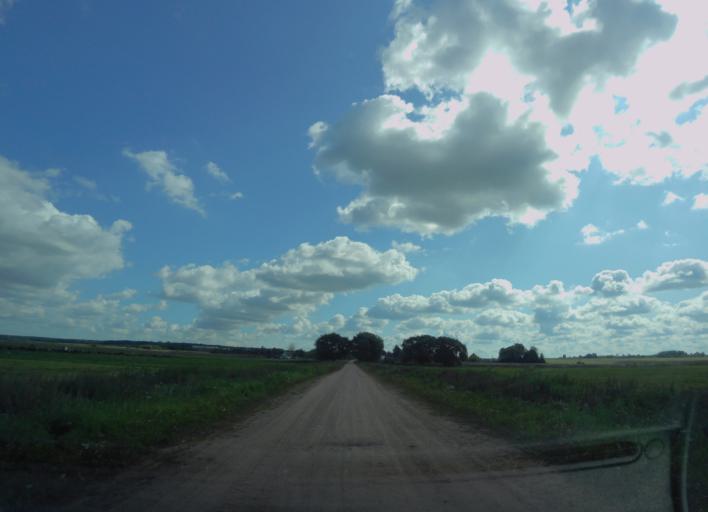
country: BY
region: Minsk
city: Zyembin
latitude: 54.3780
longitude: 28.3611
